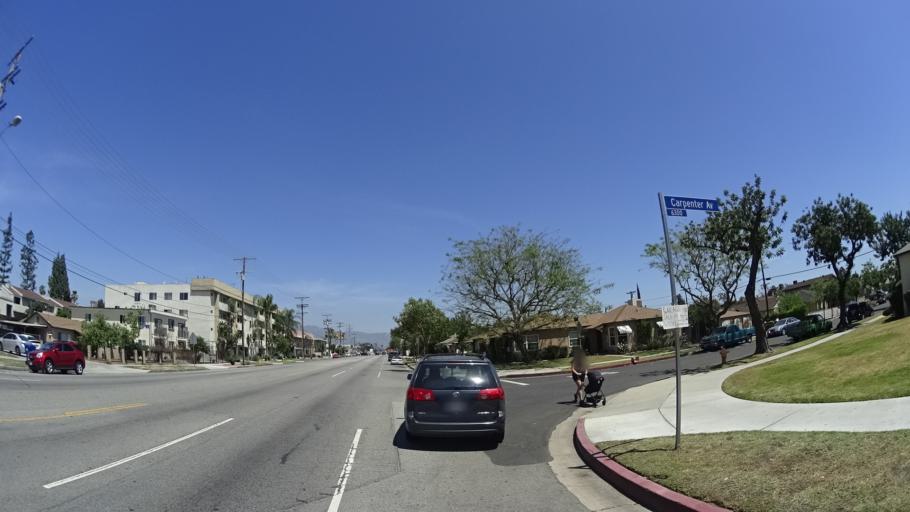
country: US
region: California
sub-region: Los Angeles County
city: North Hollywood
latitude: 34.1866
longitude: -118.3914
